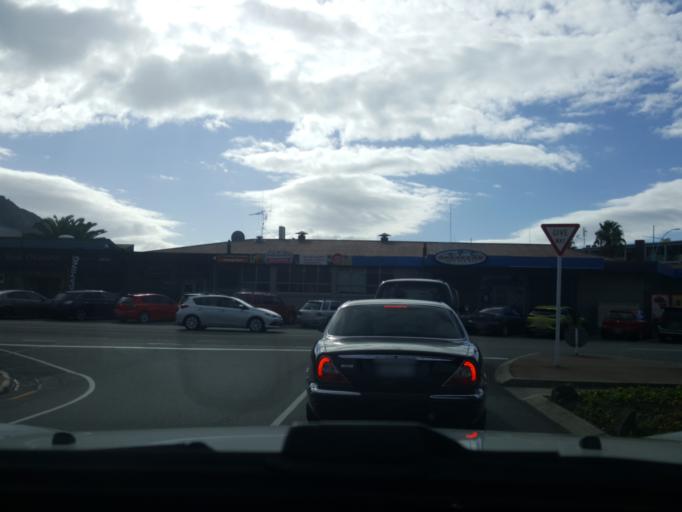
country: NZ
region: Bay of Plenty
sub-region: Tauranga City
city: Tauranga
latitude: -37.6429
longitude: 176.1856
